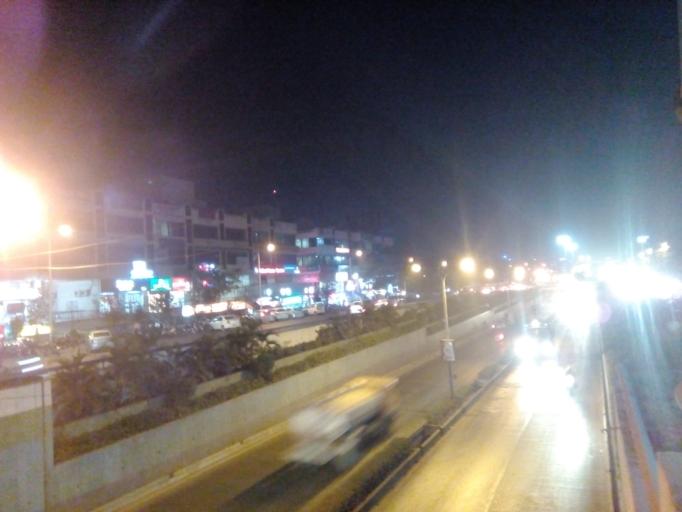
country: IN
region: Maharashtra
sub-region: Pune Division
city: Pimpri
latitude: 18.6281
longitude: 73.8042
